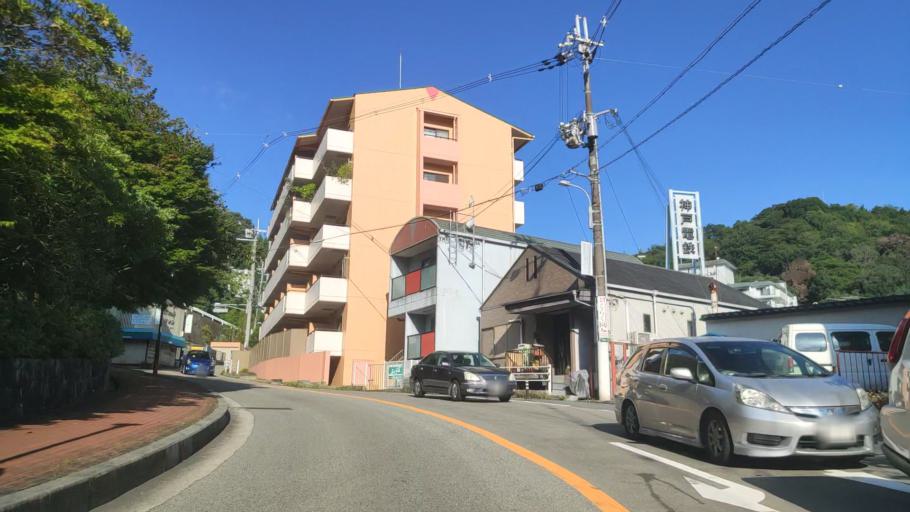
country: JP
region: Hyogo
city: Sandacho
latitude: 34.7989
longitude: 135.2466
